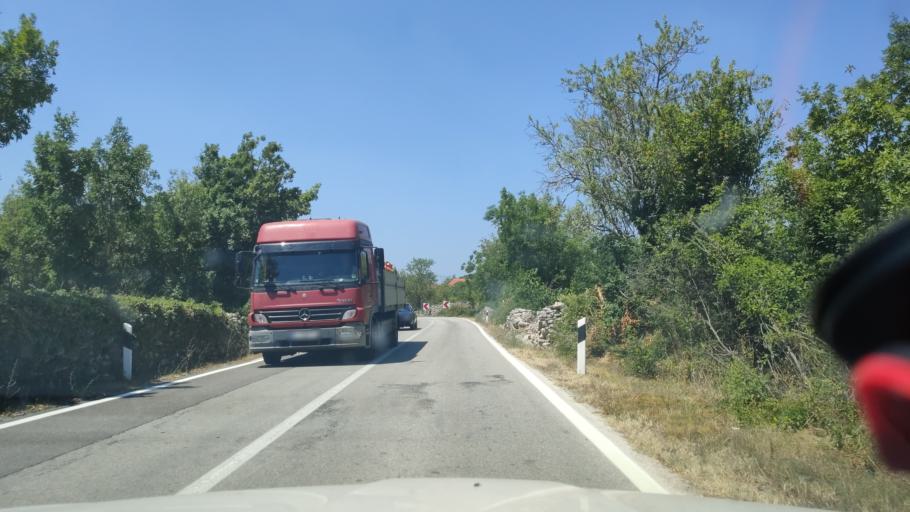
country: HR
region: Sibensko-Kniniska
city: Kistanje
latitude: 44.0046
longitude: 15.9983
